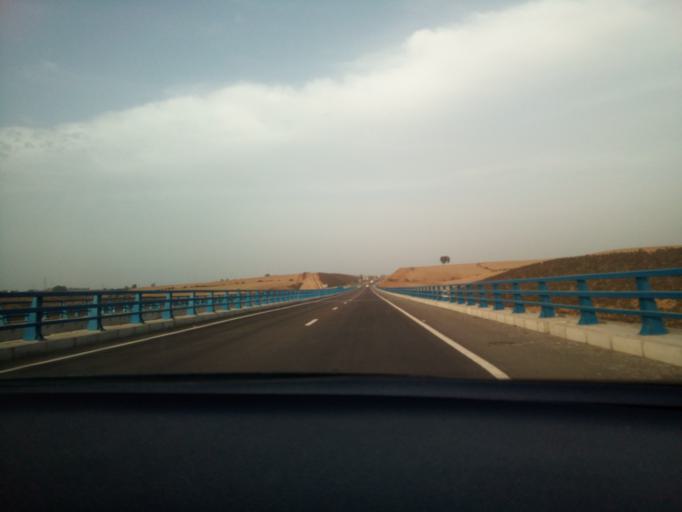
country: MA
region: Rabat-Sale-Zemmour-Zaer
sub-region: Skhirate-Temara
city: Temara
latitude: 33.8542
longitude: -6.8246
